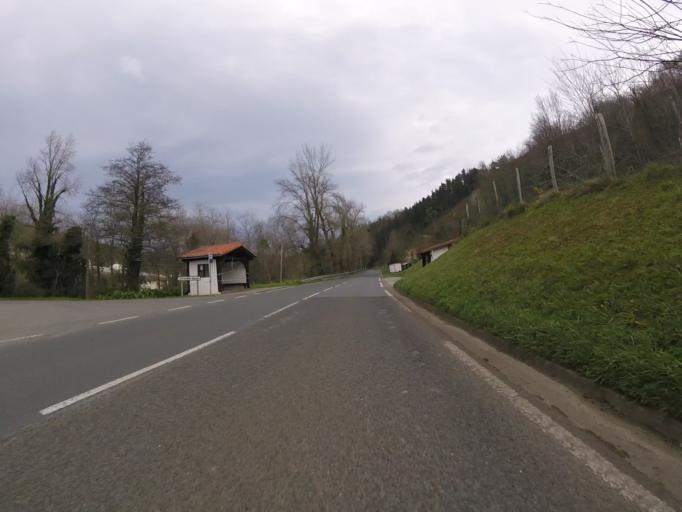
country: ES
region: Basque Country
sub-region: Provincia de Guipuzcoa
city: Aizarnazabal
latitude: 43.2657
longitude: -2.2351
